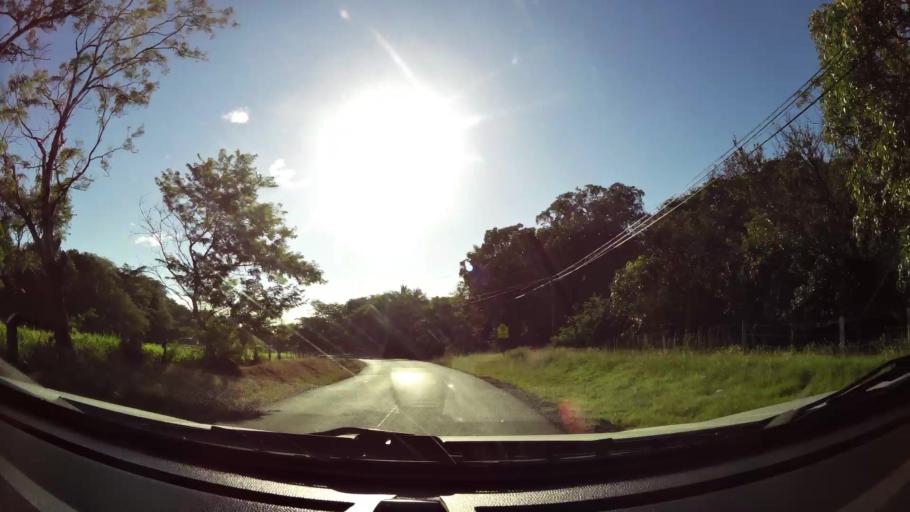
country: CR
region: Guanacaste
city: Sardinal
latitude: 10.4844
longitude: -85.6207
